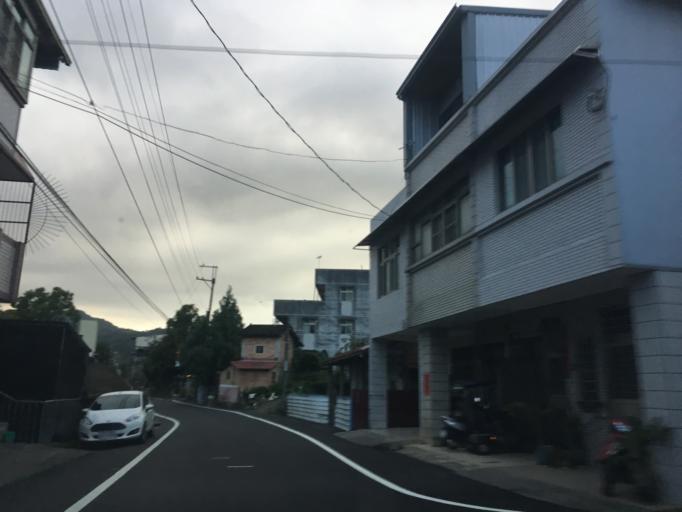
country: TW
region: Taiwan
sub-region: Nantou
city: Puli
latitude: 23.9083
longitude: 120.9245
